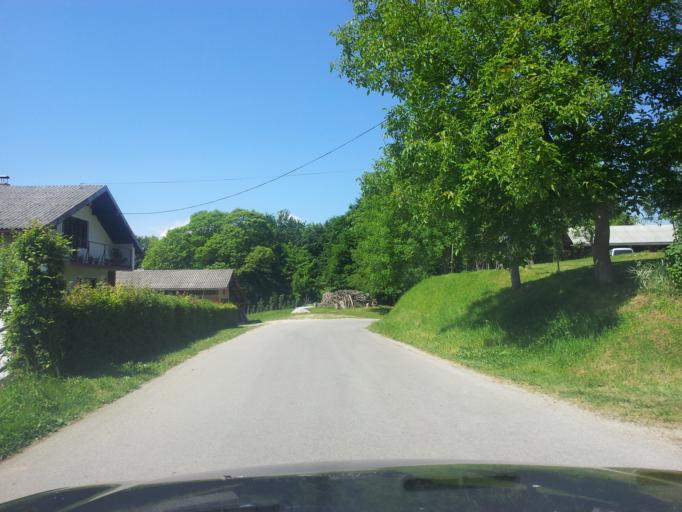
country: HR
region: Karlovacka
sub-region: Grad Karlovac
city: Karlovac
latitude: 45.4833
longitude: 15.4883
